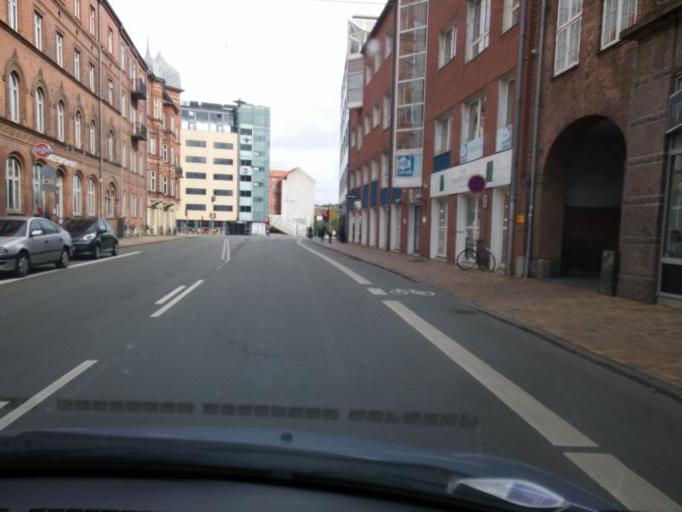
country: DK
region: South Denmark
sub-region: Odense Kommune
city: Odense
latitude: 55.4002
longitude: 10.3888
